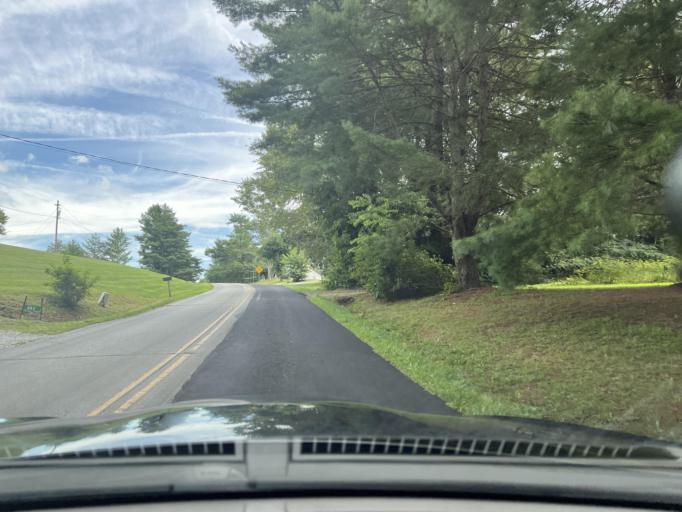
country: US
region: North Carolina
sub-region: Henderson County
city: Fruitland
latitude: 35.3934
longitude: -82.3819
